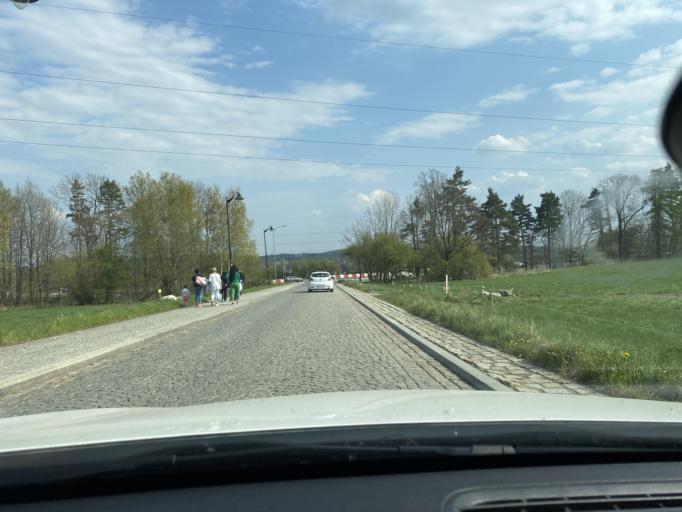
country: PL
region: Lower Silesian Voivodeship
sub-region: Powiat swidnicki
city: Swiebodzice
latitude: 50.8380
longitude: 16.3072
